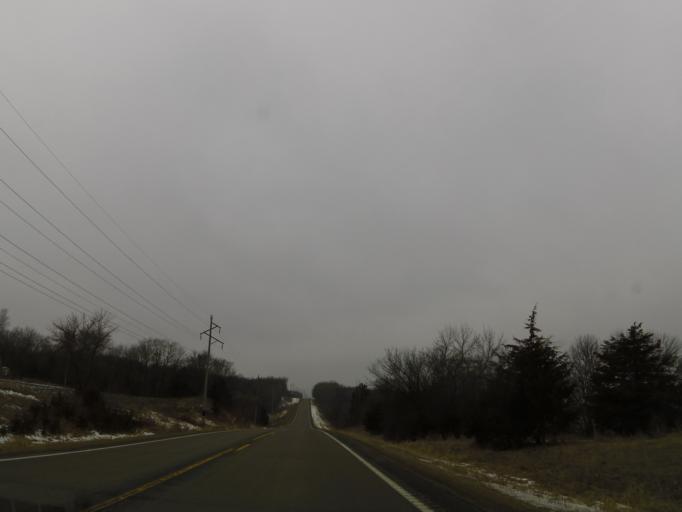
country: US
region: Minnesota
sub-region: Scott County
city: Prior Lake
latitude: 44.6752
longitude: -93.4221
